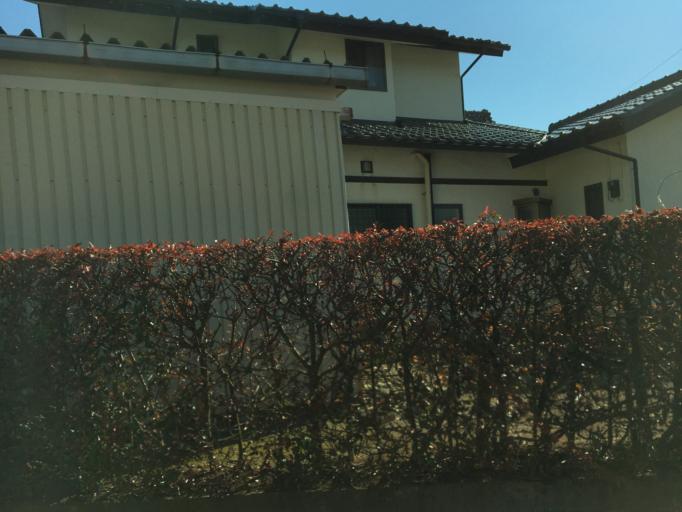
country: JP
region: Saitama
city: Sakado
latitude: 35.9628
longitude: 139.3619
